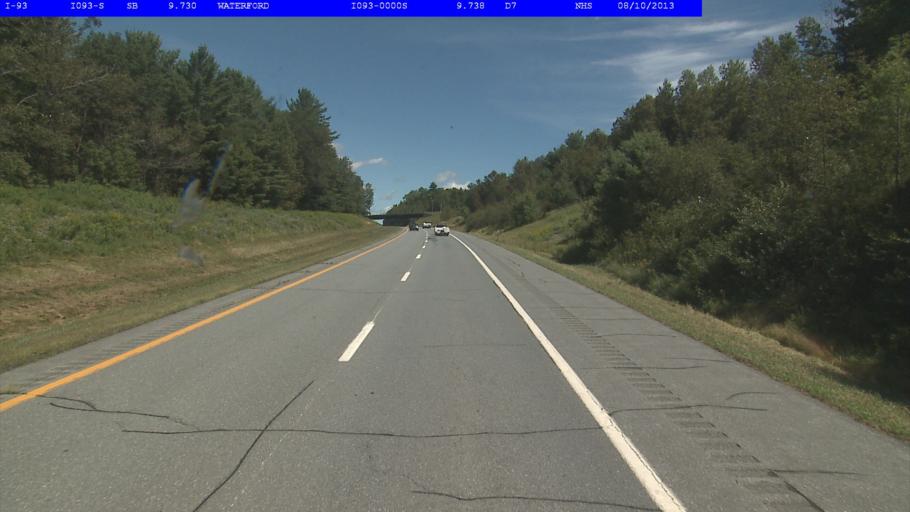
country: US
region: Vermont
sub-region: Caledonia County
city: Saint Johnsbury
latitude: 44.4079
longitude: -71.9919
